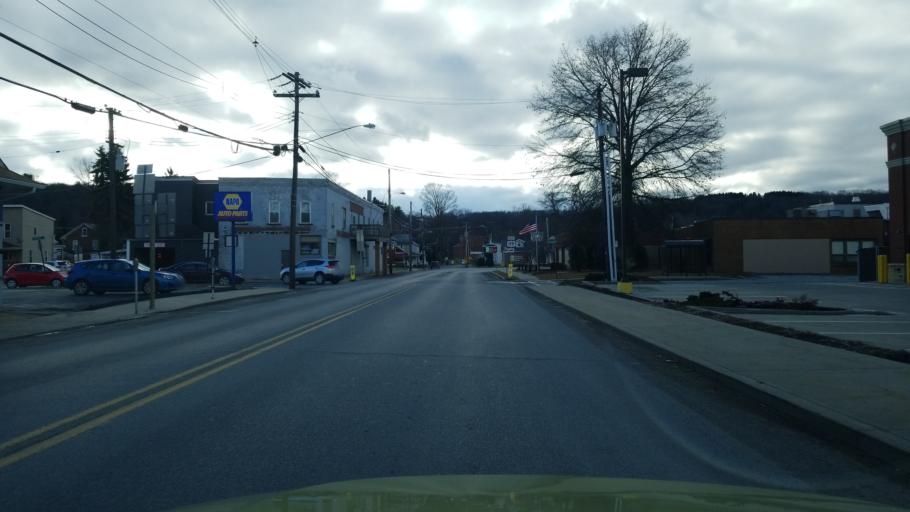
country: US
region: Pennsylvania
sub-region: Jefferson County
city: Punxsutawney
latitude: 40.9427
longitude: -78.9723
